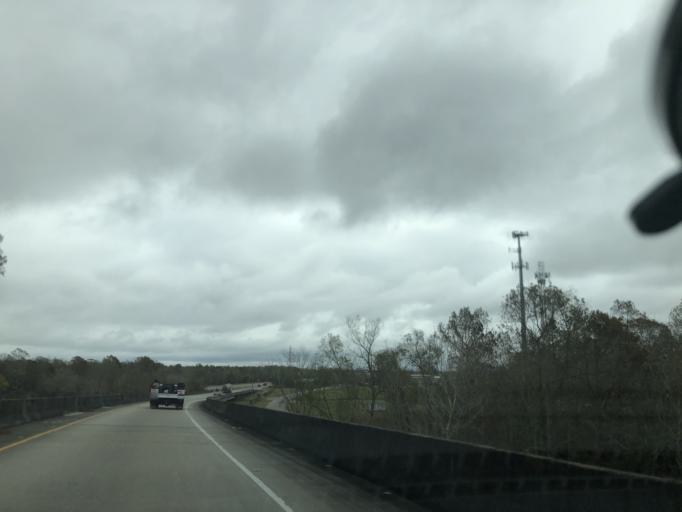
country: US
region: Louisiana
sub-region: Saint Charles Parish
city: Saint Rose
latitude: 29.9738
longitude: -90.3180
